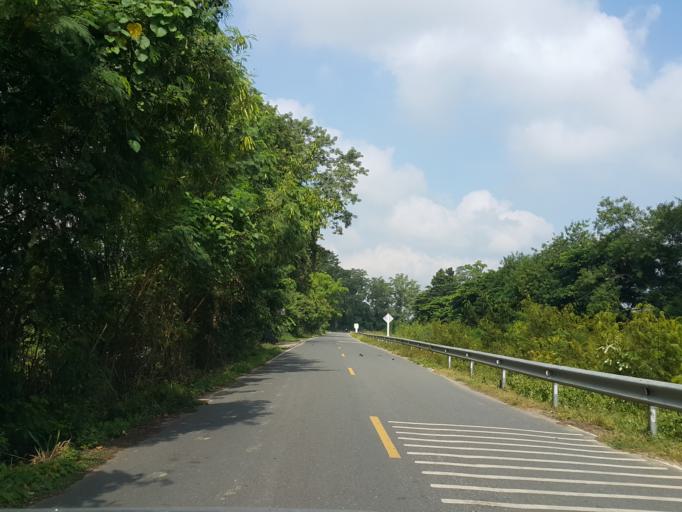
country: TH
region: Chiang Mai
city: San Sai
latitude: 18.9179
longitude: 99.0040
